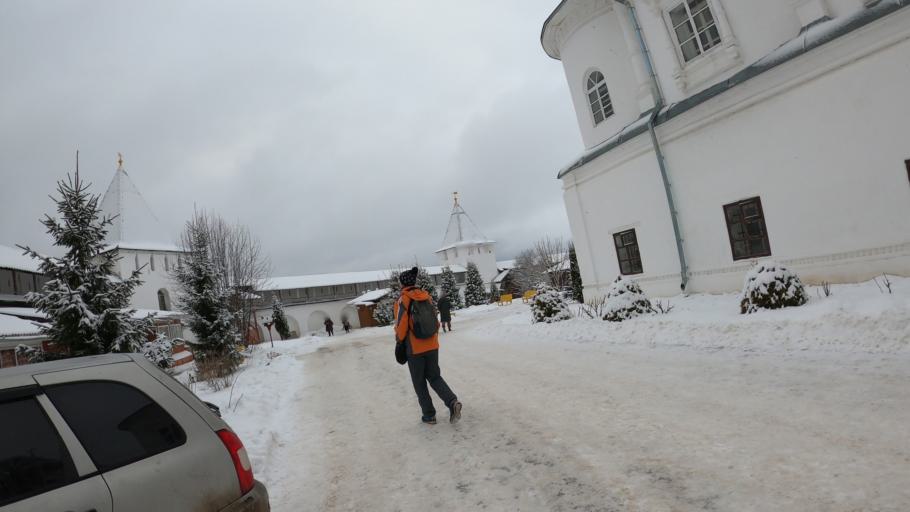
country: RU
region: Jaroslavl
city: Pereslavl'-Zalesskiy
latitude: 56.7609
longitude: 38.8594
